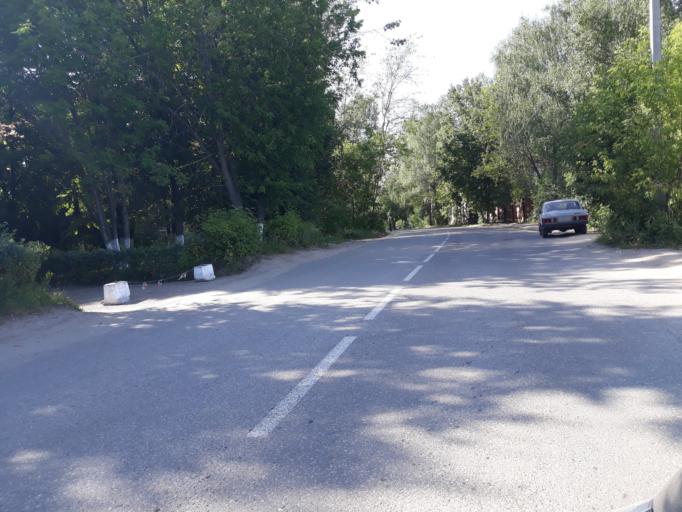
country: RU
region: Jaroslavl
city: Yaroslavl
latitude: 57.5948
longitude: 39.8600
